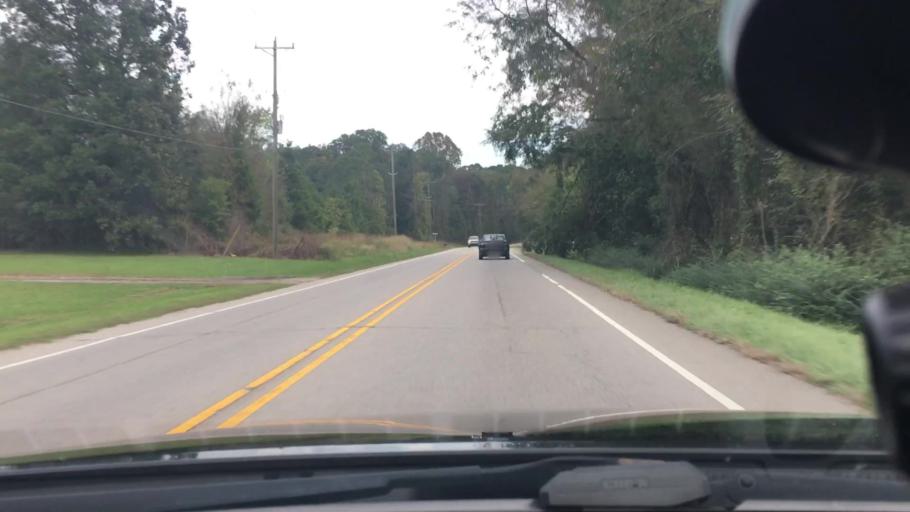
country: US
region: North Carolina
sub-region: Moore County
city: Robbins
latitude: 35.4042
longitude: -79.5712
